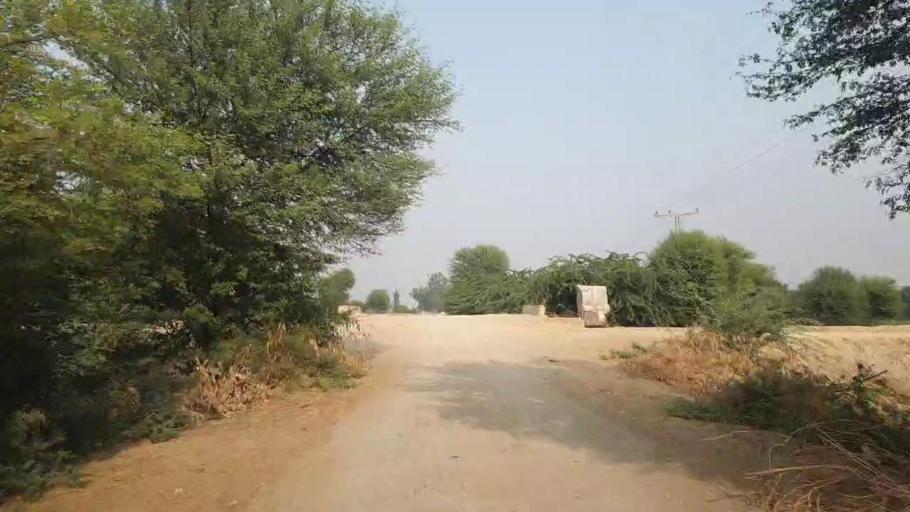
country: PK
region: Sindh
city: Sann
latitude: 26.0687
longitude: 68.1135
